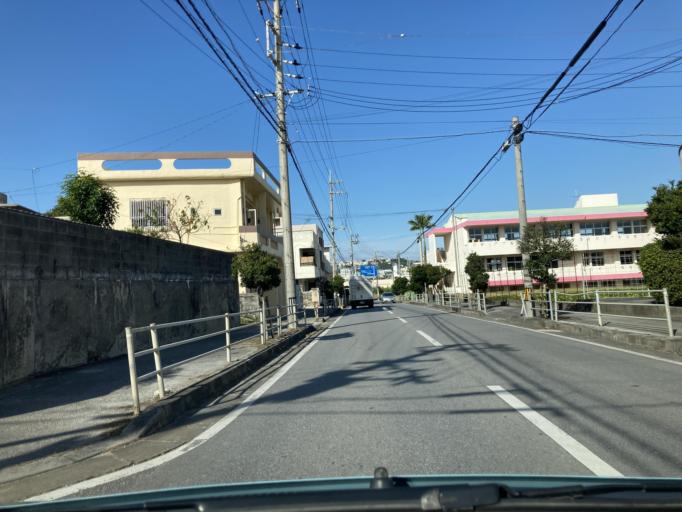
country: JP
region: Okinawa
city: Tomigusuku
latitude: 26.1839
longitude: 127.7071
